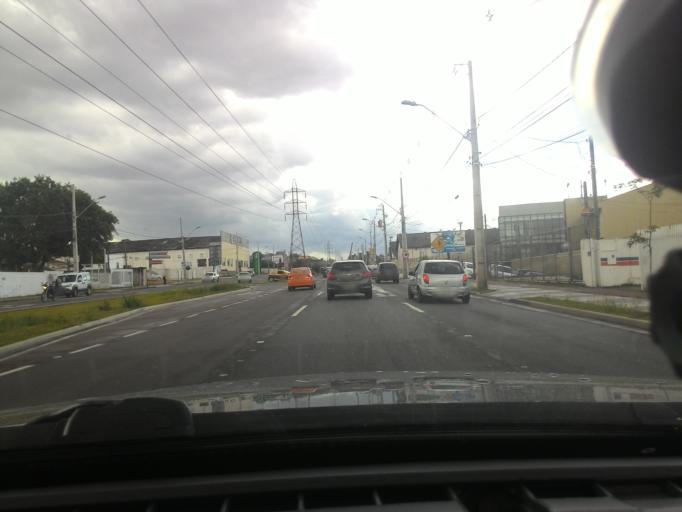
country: BR
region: Parana
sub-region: Pinhais
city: Pinhais
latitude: -25.4775
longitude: -49.2252
